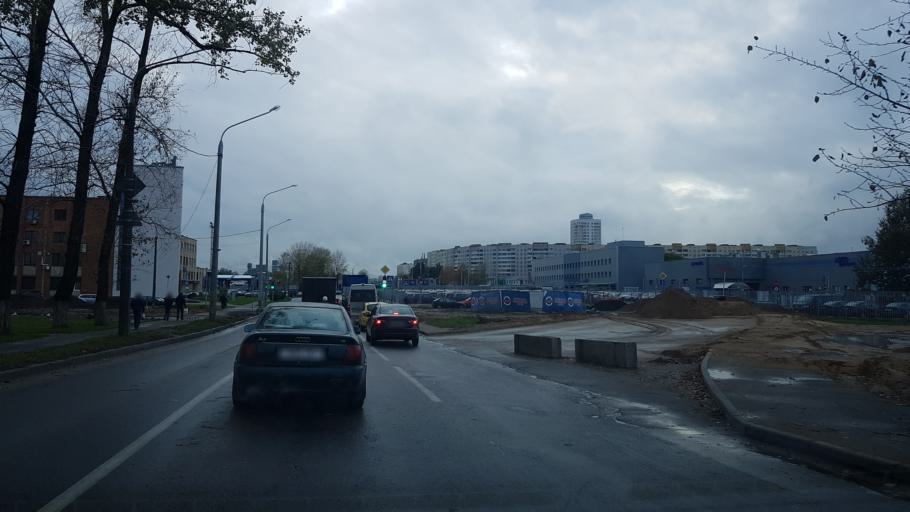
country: BY
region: Minsk
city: Syenitsa
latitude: 53.8432
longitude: 27.5405
